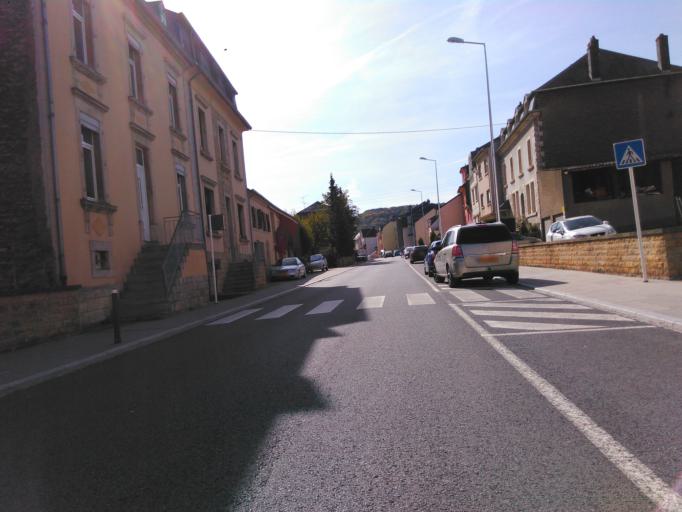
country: LU
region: Luxembourg
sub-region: Canton d'Esch-sur-Alzette
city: Kayl
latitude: 49.4835
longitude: 6.0381
